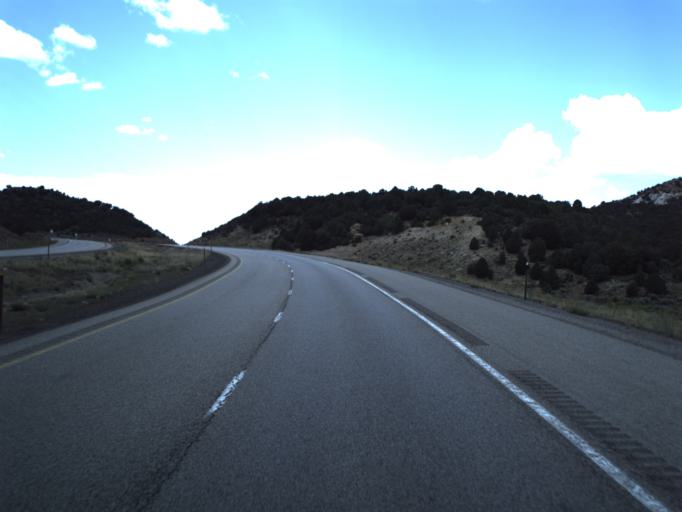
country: US
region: Utah
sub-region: Wayne County
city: Loa
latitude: 38.7770
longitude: -111.4787
